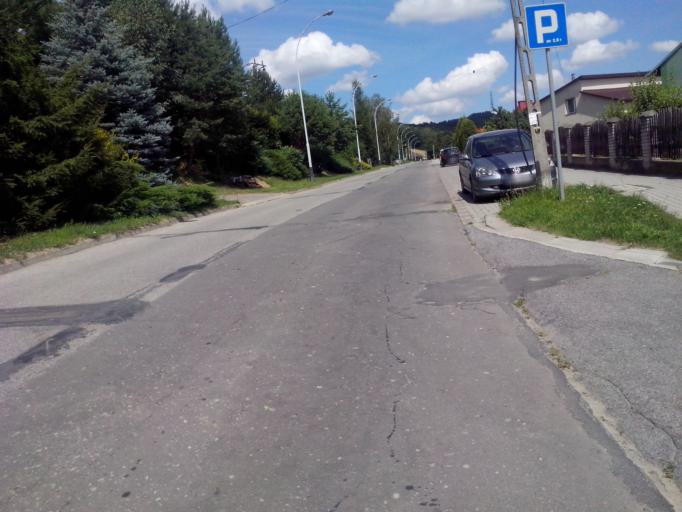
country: PL
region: Subcarpathian Voivodeship
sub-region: Powiat strzyzowski
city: Strzyzow
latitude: 49.8724
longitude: 21.7867
